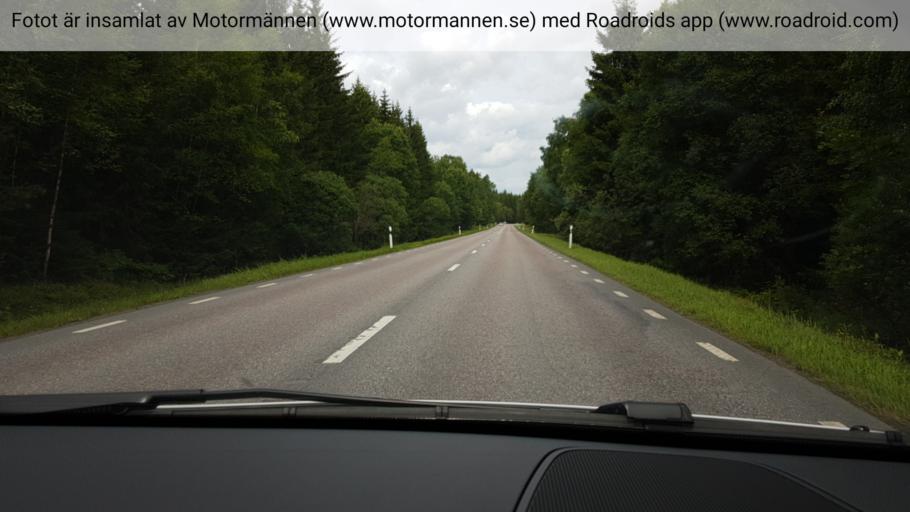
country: SE
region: Uppsala
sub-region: Osthammars Kommun
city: Gimo
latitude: 60.2070
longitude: 18.1932
